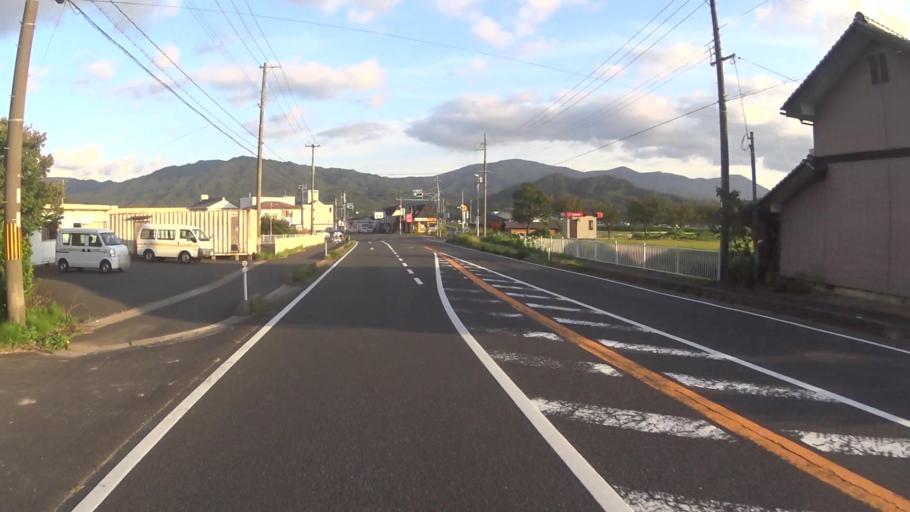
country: JP
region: Kyoto
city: Miyazu
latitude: 35.5372
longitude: 135.1136
